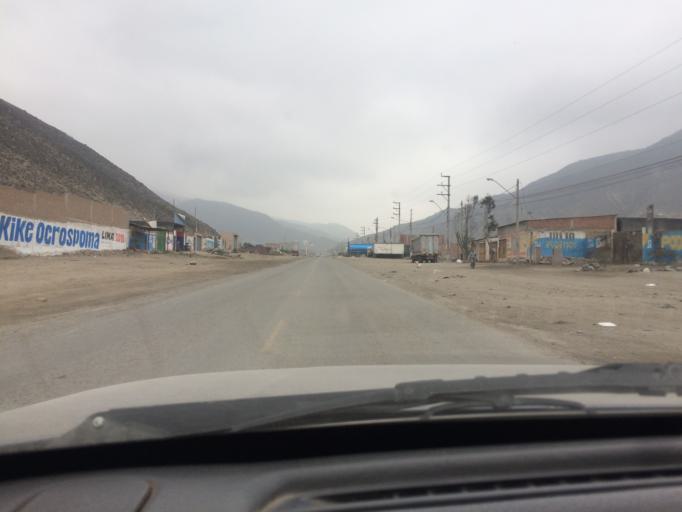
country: PE
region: Lima
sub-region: Lima
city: Cieneguilla
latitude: -12.1644
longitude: -76.8660
